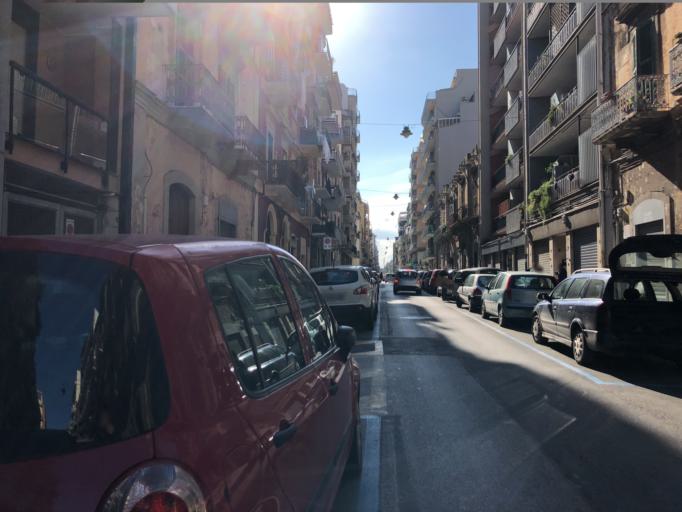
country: IT
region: Apulia
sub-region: Provincia di Bari
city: Bari
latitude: 41.1263
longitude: 16.8584
